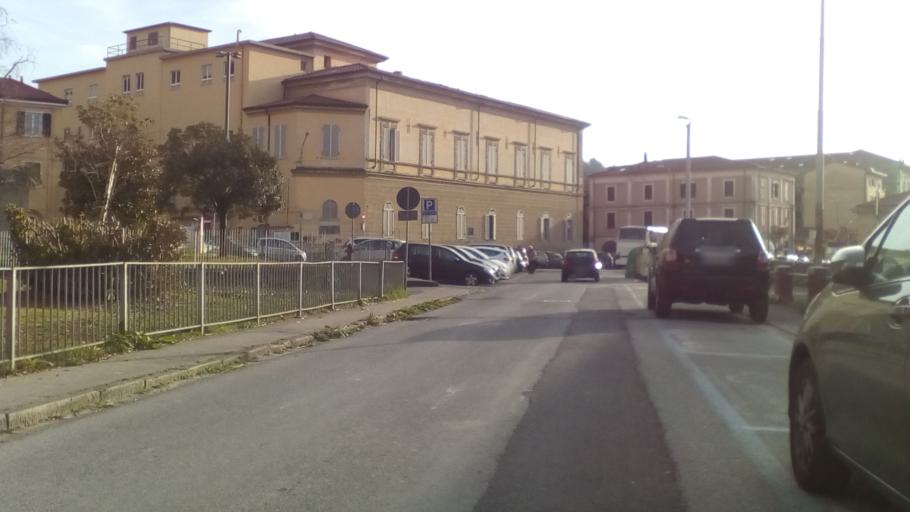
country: IT
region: Tuscany
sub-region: Provincia di Massa-Carrara
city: Carrara
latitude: 44.0801
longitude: 10.1021
